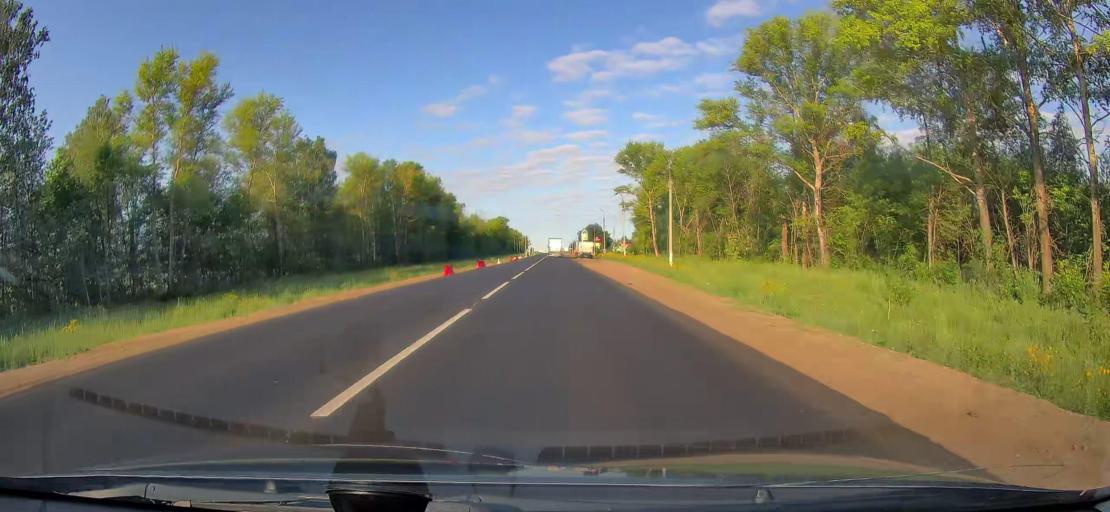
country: RU
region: Tula
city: Bol'shoye Skuratovo
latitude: 53.4364
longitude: 36.8133
